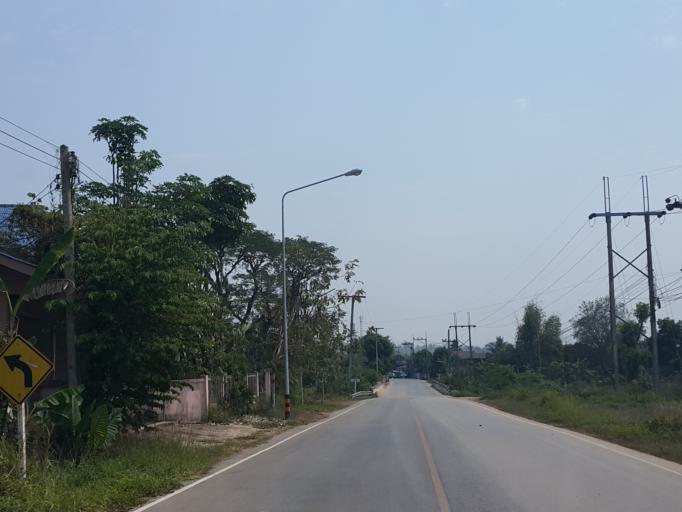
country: TH
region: Lampang
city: Chae Hom
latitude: 18.7597
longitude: 99.5606
